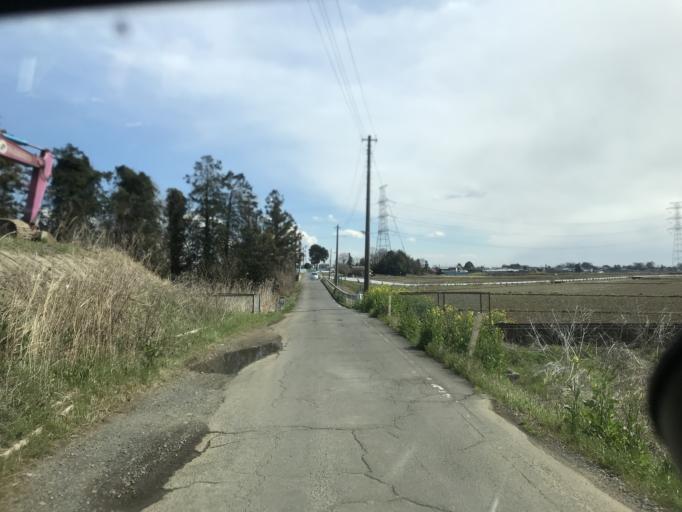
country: JP
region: Ibaraki
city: Yuki
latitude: 36.2709
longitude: 139.9096
